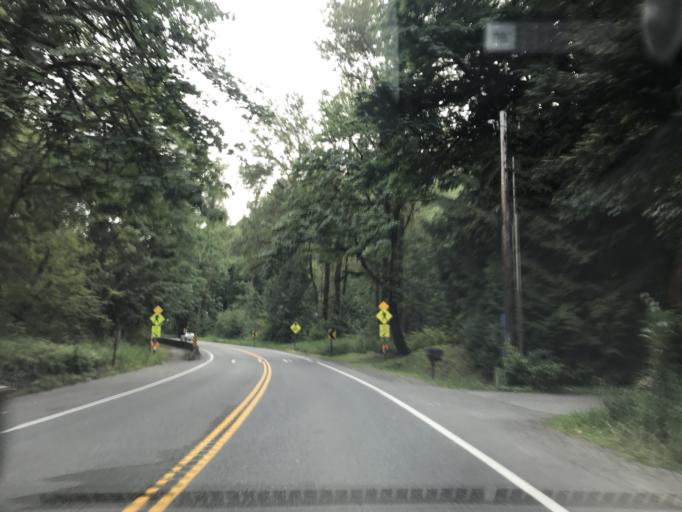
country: US
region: Washington
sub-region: King County
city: Fall City
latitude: 47.5413
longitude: -121.9076
